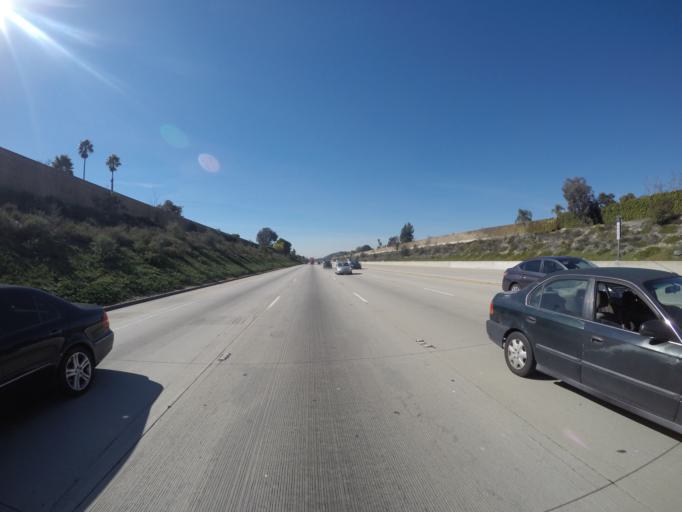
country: US
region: California
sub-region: Los Angeles County
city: Claremont
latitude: 34.1198
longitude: -117.7059
